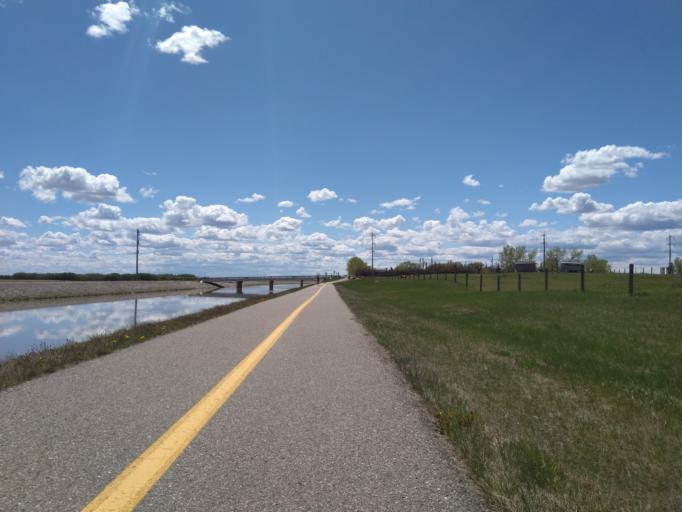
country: CA
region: Alberta
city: Chestermere
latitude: 51.0104
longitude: -113.8466
